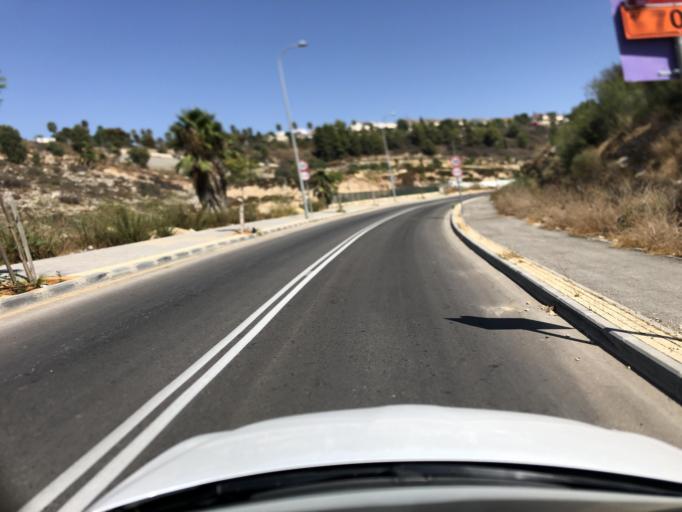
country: PS
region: West Bank
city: An Nabi Ilyas
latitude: 32.1697
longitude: 35.0045
